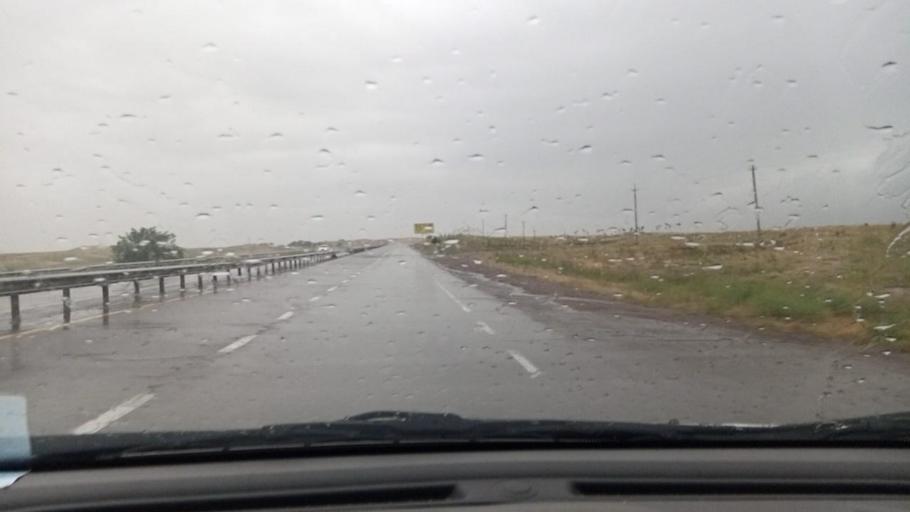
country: UZ
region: Toshkent
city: Ohangaron
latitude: 40.9725
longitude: 69.5461
